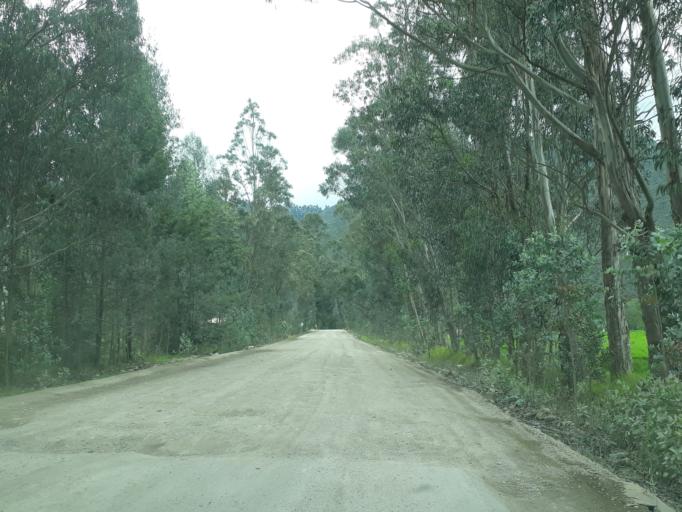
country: CO
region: Cundinamarca
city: Lenguazaque
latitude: 5.3236
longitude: -73.7471
